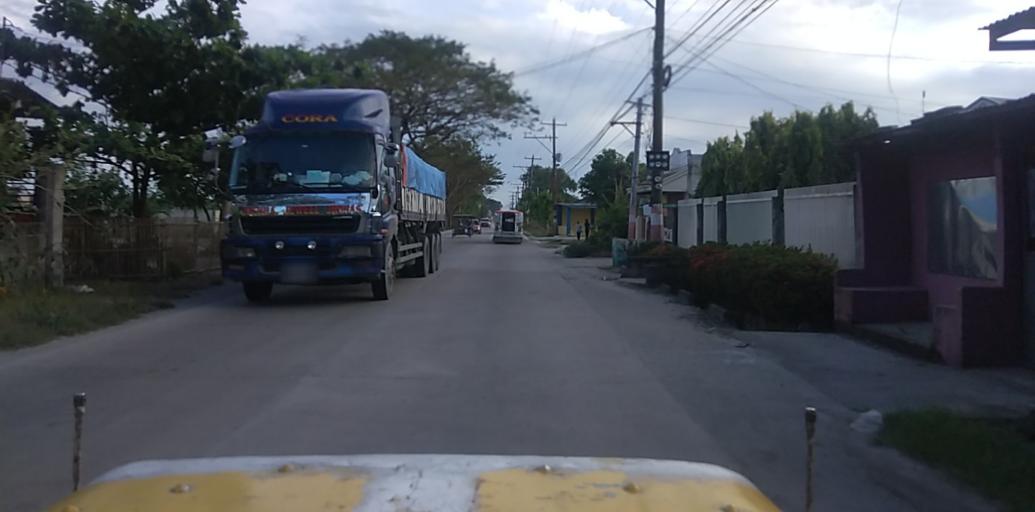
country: PH
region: Central Luzon
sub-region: Province of Pampanga
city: Anao
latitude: 15.1461
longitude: 120.6911
